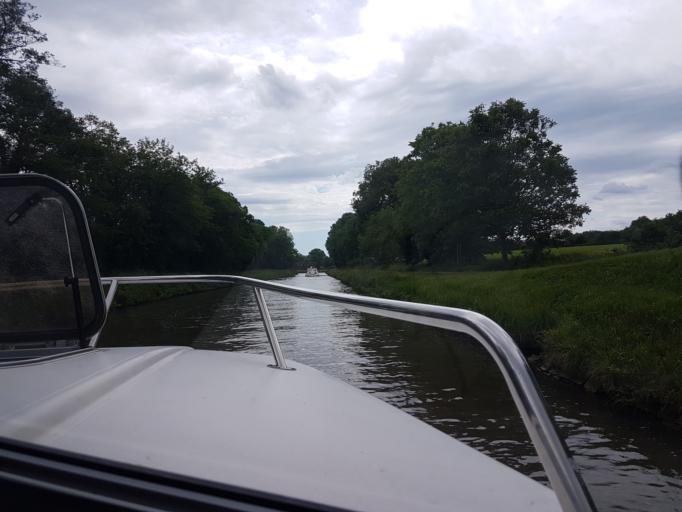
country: FR
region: Bourgogne
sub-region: Departement de la Nievre
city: Clamecy
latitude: 47.4822
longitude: 3.5242
